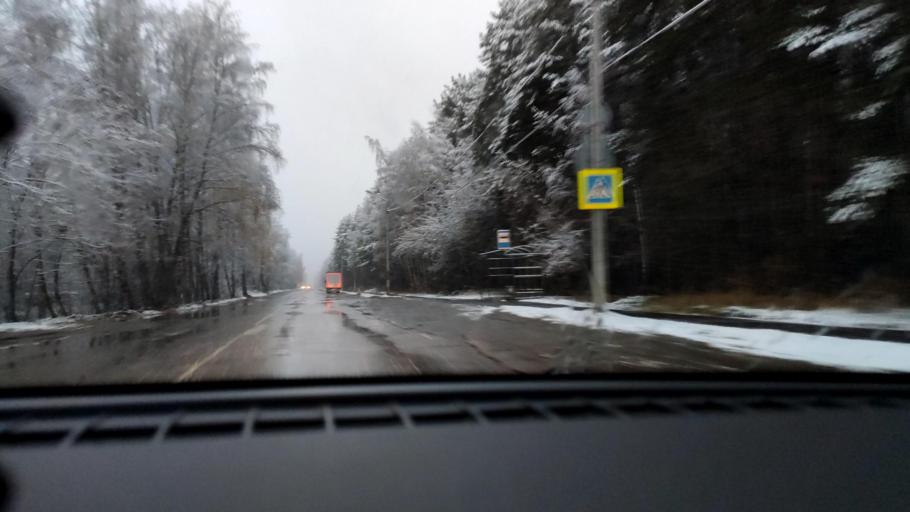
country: RU
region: Perm
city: Overyata
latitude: 58.0133
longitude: 55.9179
